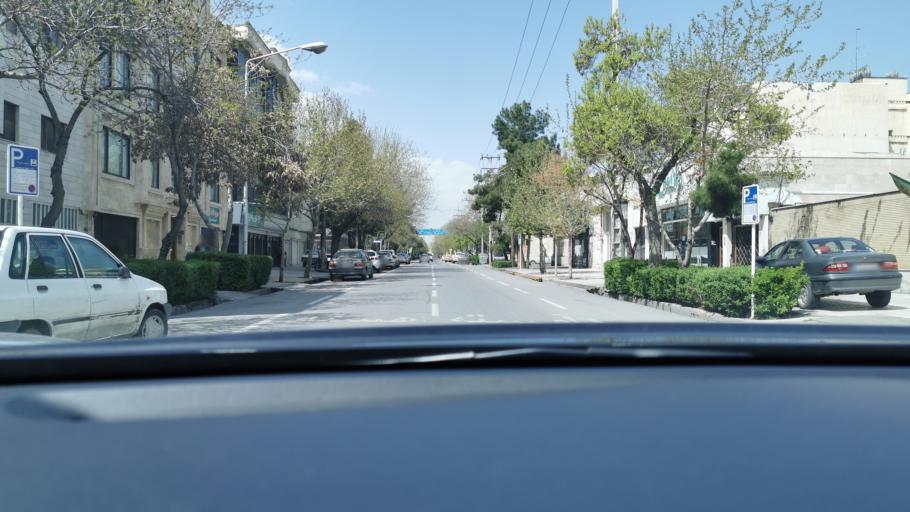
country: IR
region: Razavi Khorasan
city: Mashhad
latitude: 36.2988
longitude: 59.5906
